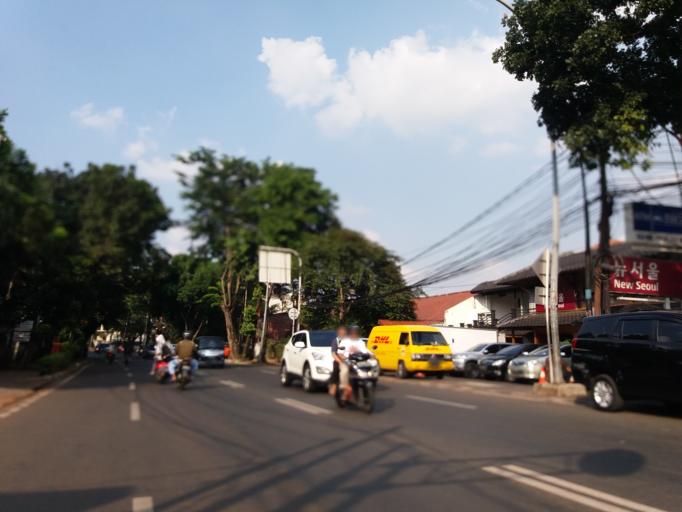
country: ID
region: Jakarta Raya
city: Jakarta
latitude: -6.2447
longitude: 106.8098
